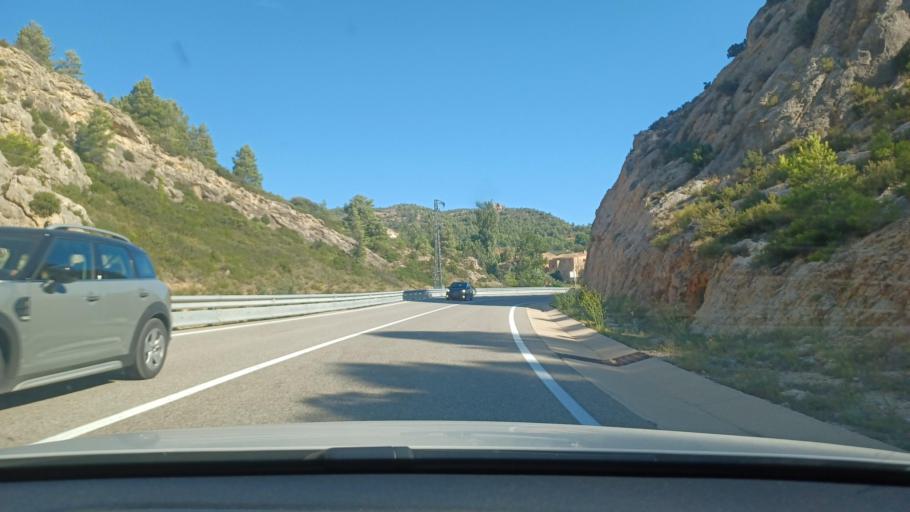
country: ES
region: Catalonia
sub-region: Provincia de Tarragona
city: Bot
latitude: 40.9796
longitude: 0.4072
